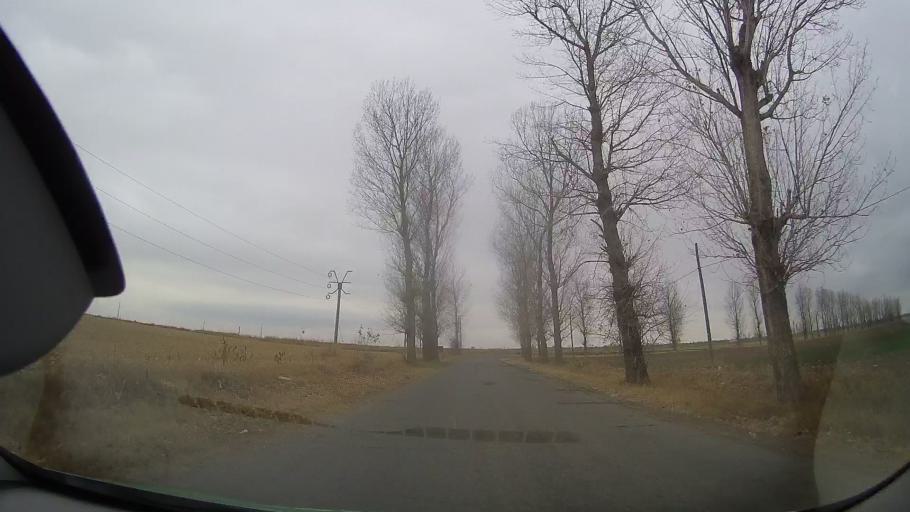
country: RO
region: Buzau
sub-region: Comuna Rusetu
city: Rusetu
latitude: 44.9440
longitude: 27.2328
